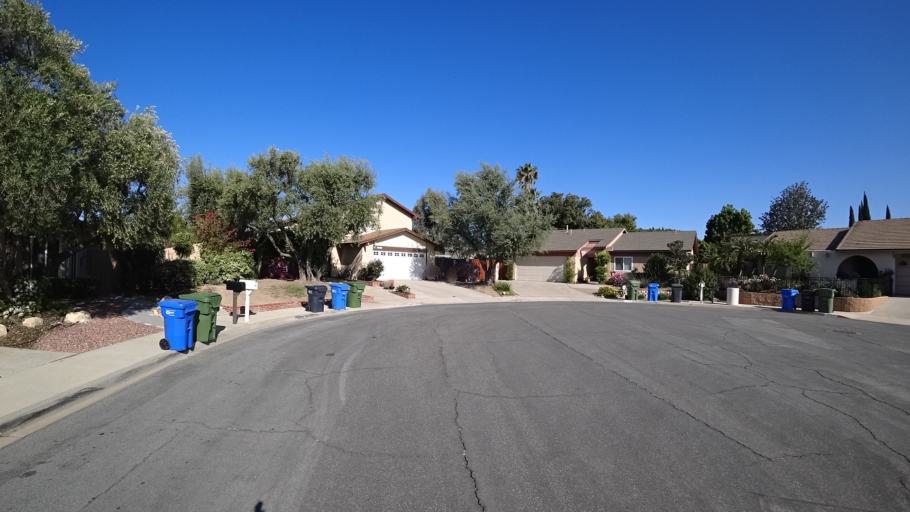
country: US
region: California
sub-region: Ventura County
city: Thousand Oaks
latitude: 34.2099
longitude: -118.8380
